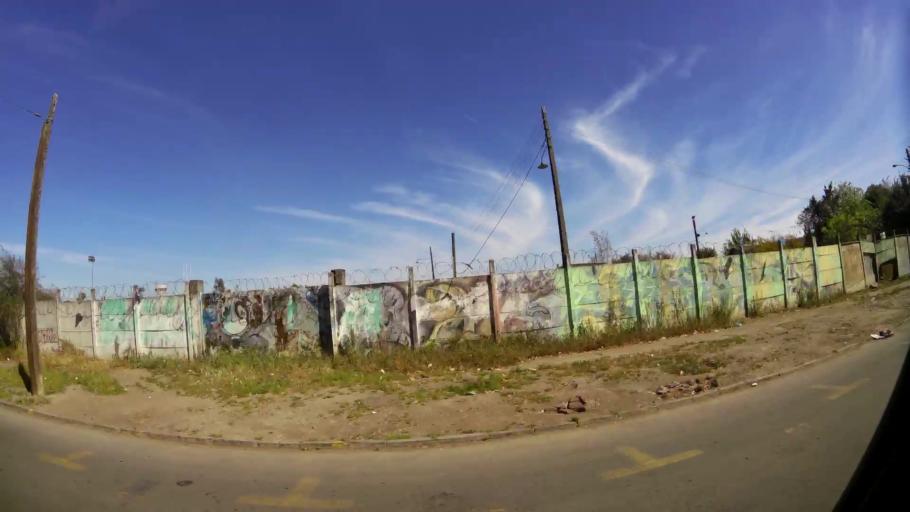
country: CL
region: Santiago Metropolitan
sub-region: Provincia de Santiago
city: Lo Prado
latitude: -33.4947
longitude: -70.7146
